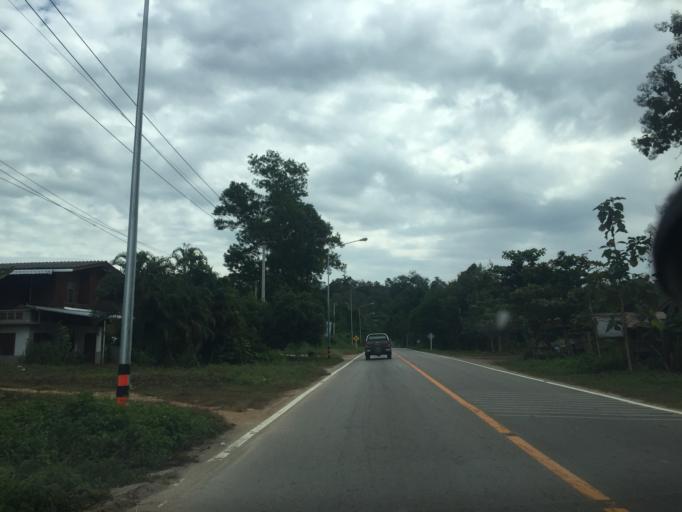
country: TH
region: Lampang
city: Mueang Pan
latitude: 18.8204
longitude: 99.5077
